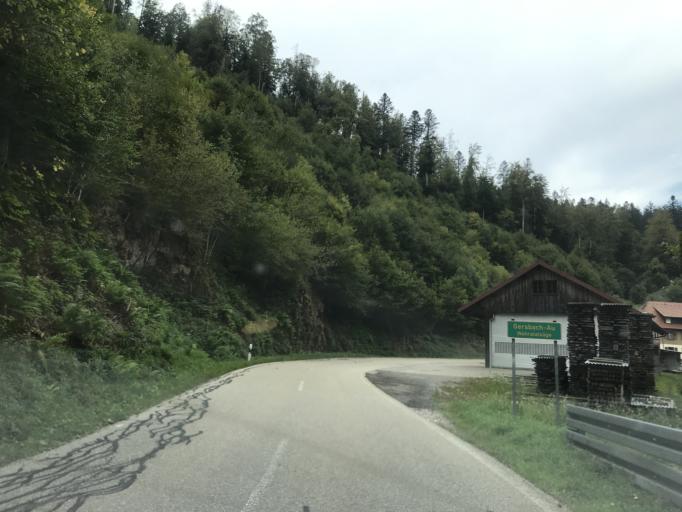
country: DE
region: Baden-Wuerttemberg
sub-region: Freiburg Region
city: Herrischried
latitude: 47.6915
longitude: 7.9685
